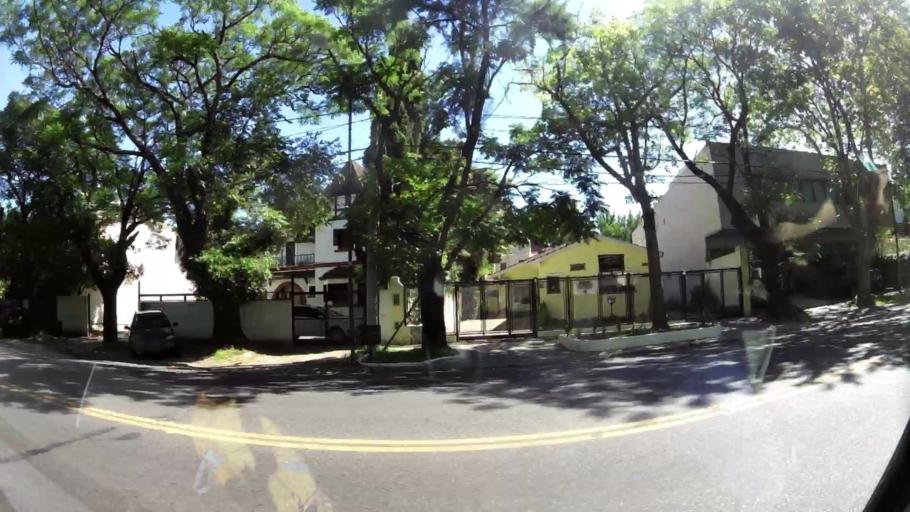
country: AR
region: Buenos Aires
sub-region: Partido de San Isidro
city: San Isidro
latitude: -34.4638
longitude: -58.5162
